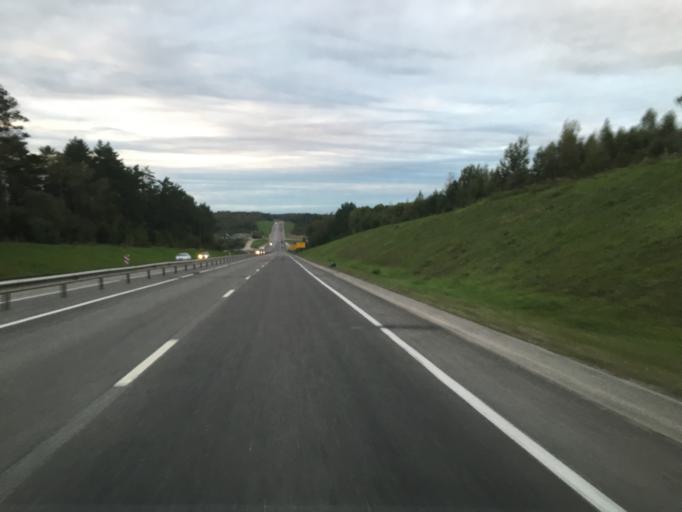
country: RU
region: Kaluga
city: Kaluga
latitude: 54.5949
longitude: 36.3253
